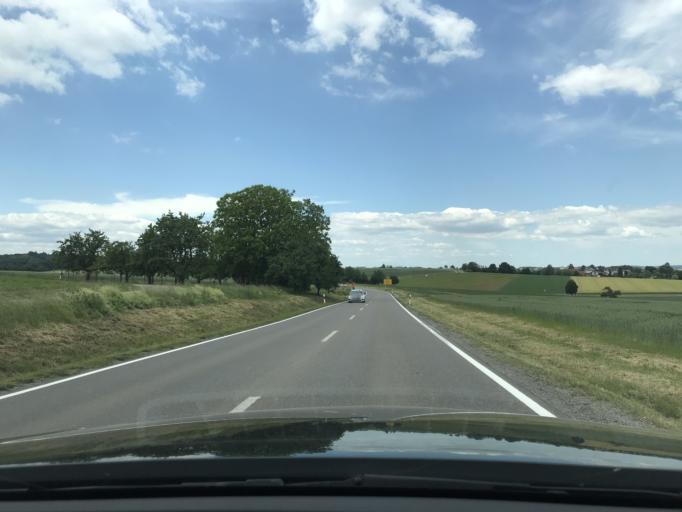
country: DE
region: Baden-Wuerttemberg
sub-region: Regierungsbezirk Stuttgart
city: Schwaikheim
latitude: 48.8901
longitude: 9.3679
